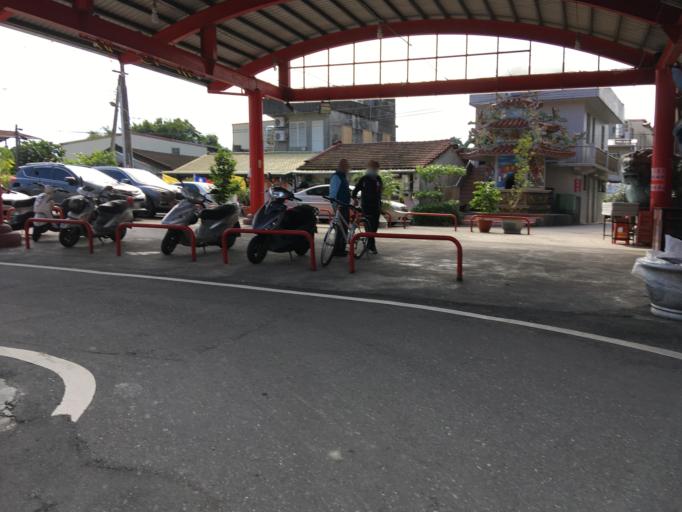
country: TW
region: Taiwan
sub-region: Yilan
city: Yilan
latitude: 24.8375
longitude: 121.7837
